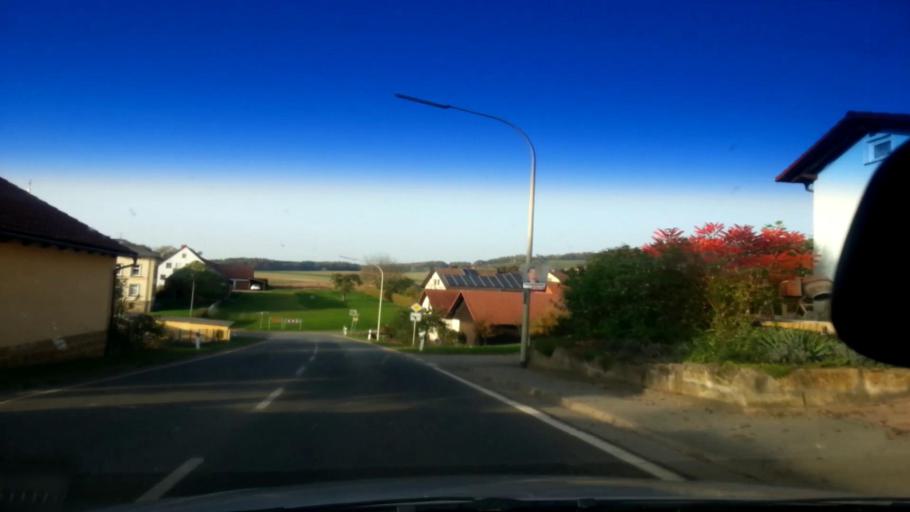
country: DE
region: Bavaria
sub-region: Upper Franconia
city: Schesslitz
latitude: 50.0027
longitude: 11.0190
